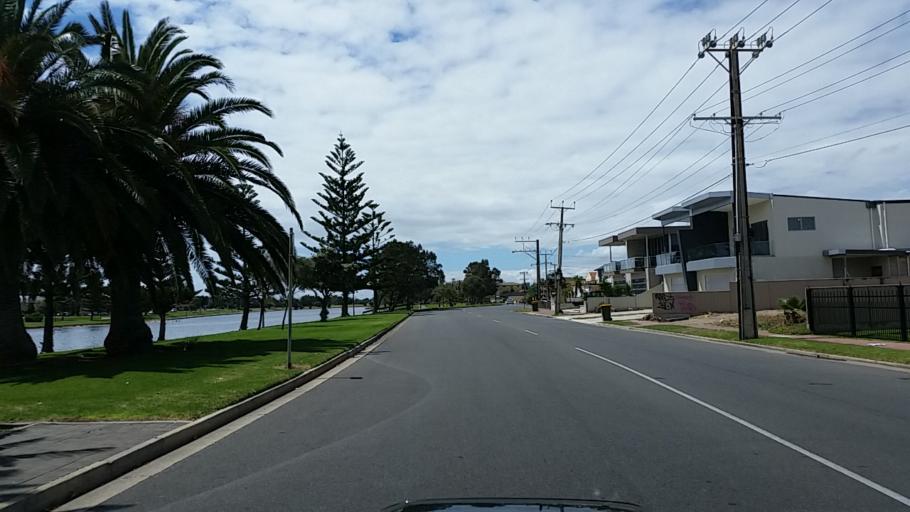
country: AU
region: South Australia
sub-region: Adelaide
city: Glenelg
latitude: -34.9690
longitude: 138.5139
